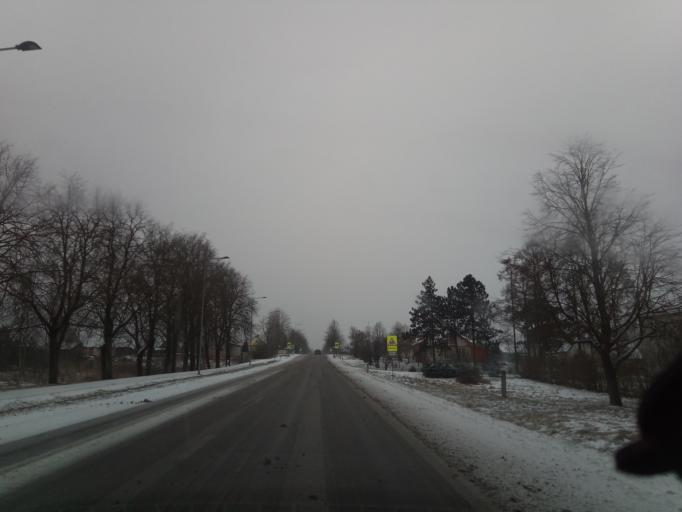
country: LT
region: Vilnius County
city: Ukmerge
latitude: 55.3112
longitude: 24.8680
